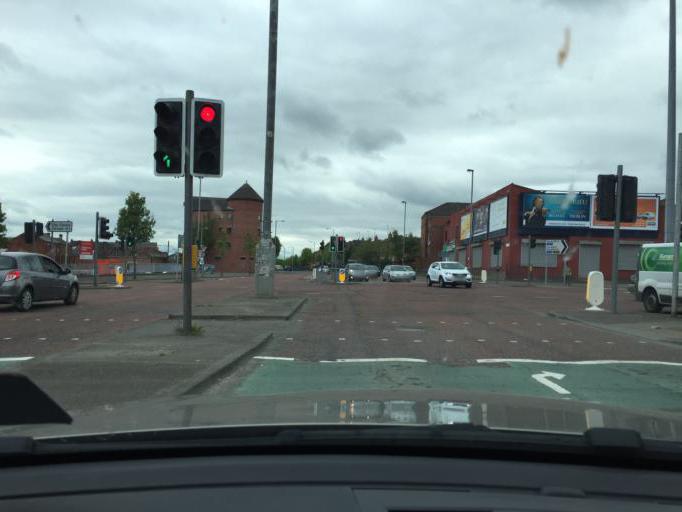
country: GB
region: Northern Ireland
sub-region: City of Belfast
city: Belfast
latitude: 54.6057
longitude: -5.9322
